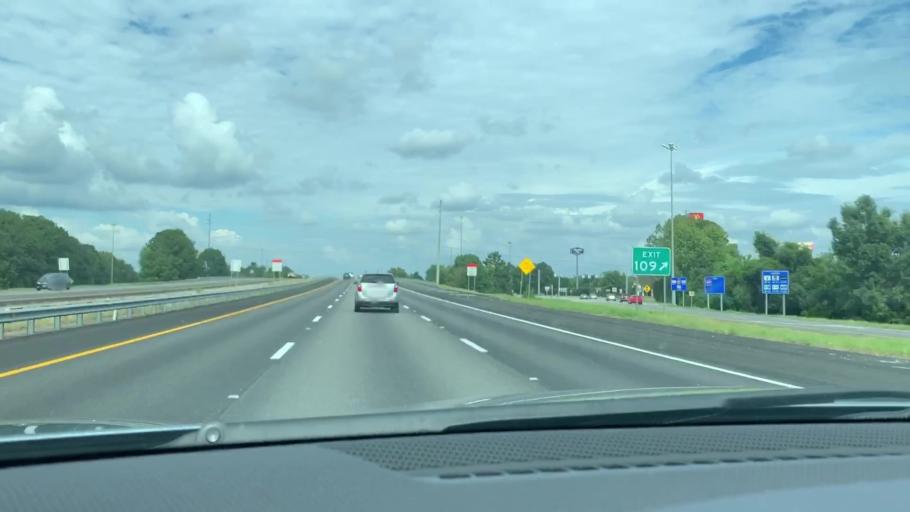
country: US
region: Georgia
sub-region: Chatham County
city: Port Wentworth
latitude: 32.1879
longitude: -81.1964
